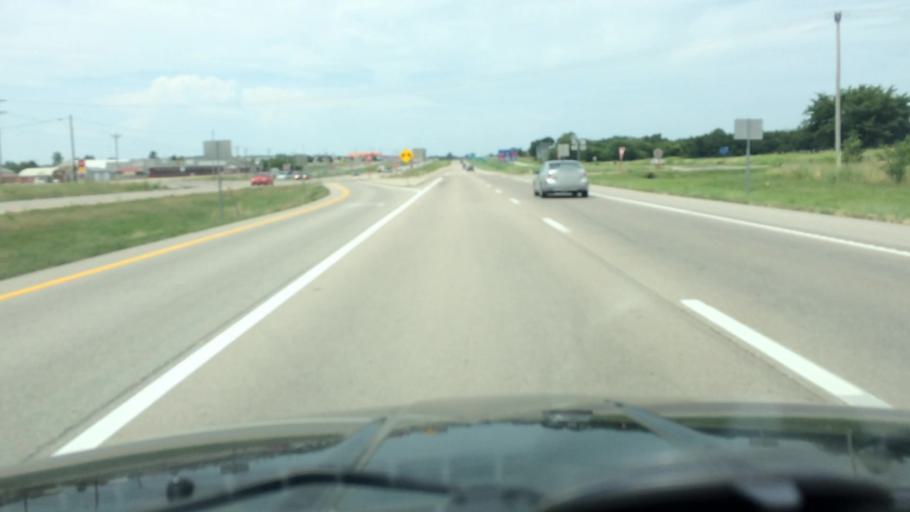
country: US
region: Missouri
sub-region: Polk County
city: Bolivar
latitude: 37.5523
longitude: -93.3867
